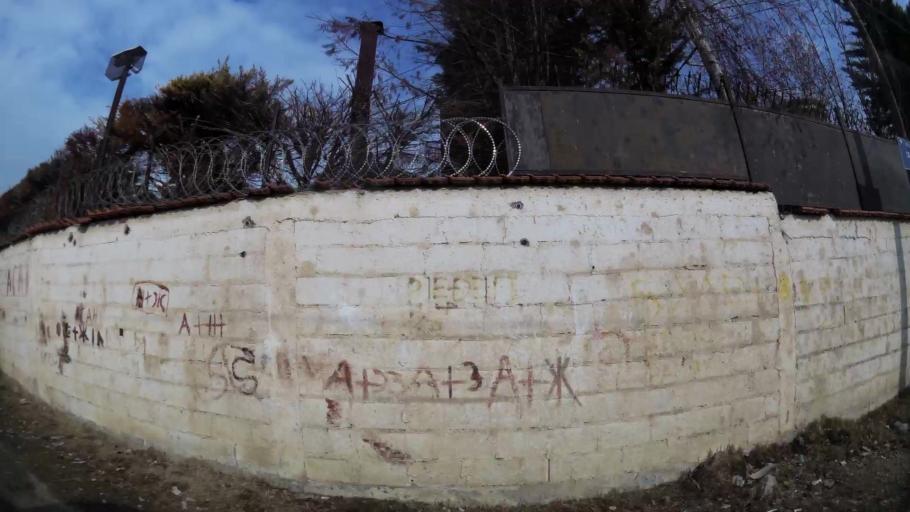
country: MK
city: Krushopek
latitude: 42.0162
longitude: 21.3833
